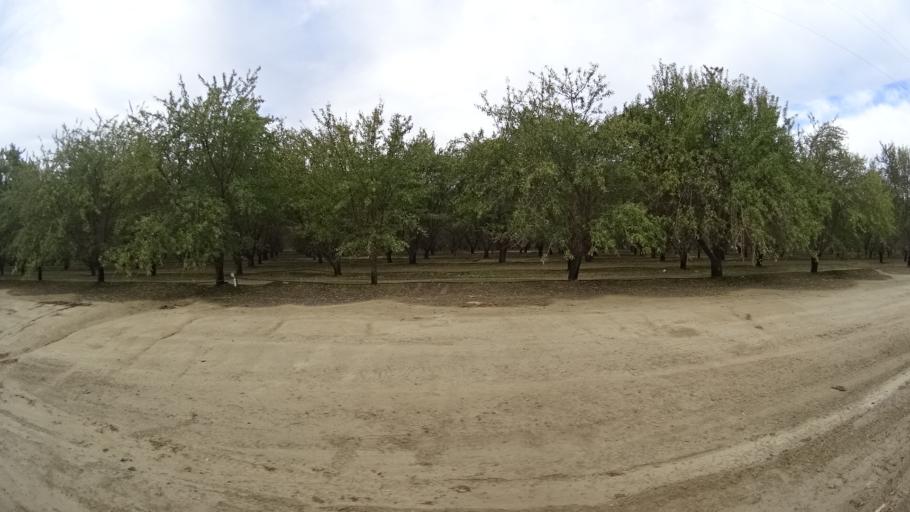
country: US
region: California
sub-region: Kern County
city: Rosedale
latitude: 35.4363
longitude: -119.1721
